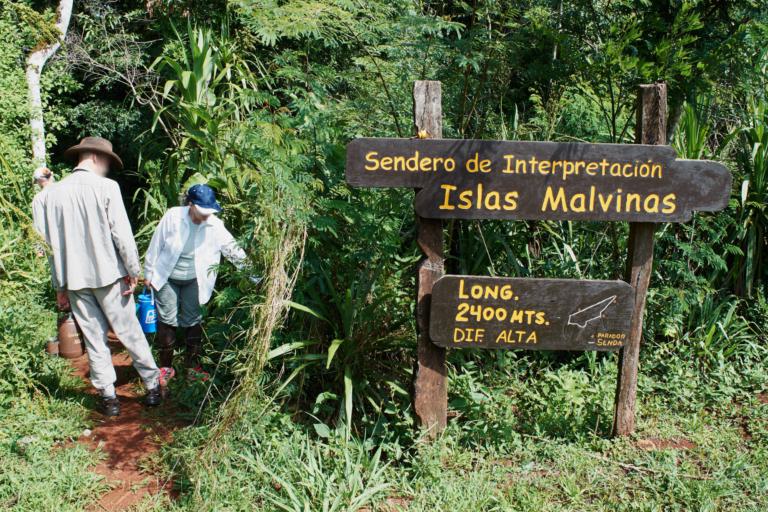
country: AR
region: Misiones
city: Colonia Wanda
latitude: -25.8577
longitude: -54.1697
